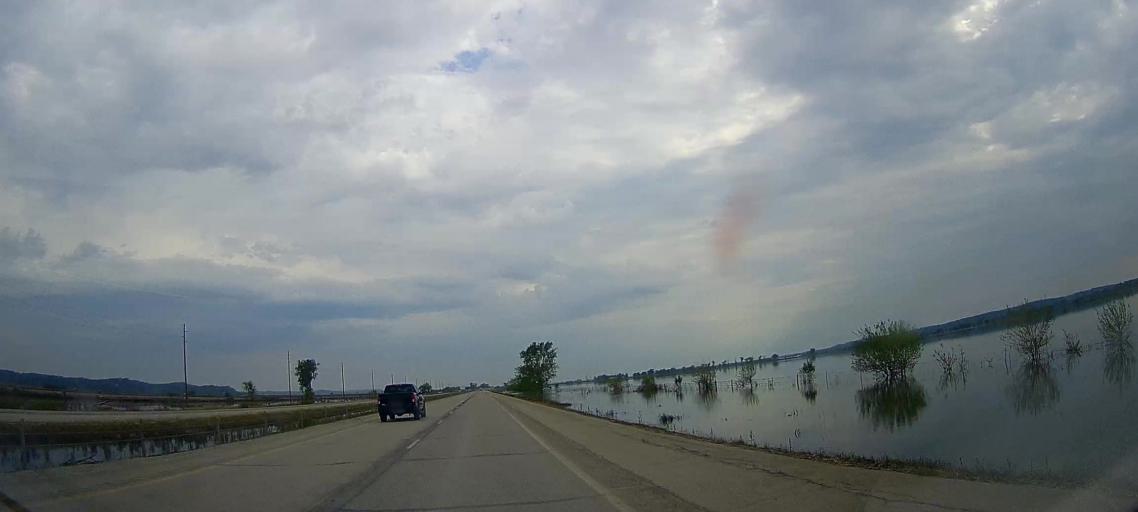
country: US
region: Iowa
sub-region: Harrison County
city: Missouri Valley
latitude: 41.4441
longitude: -95.8998
